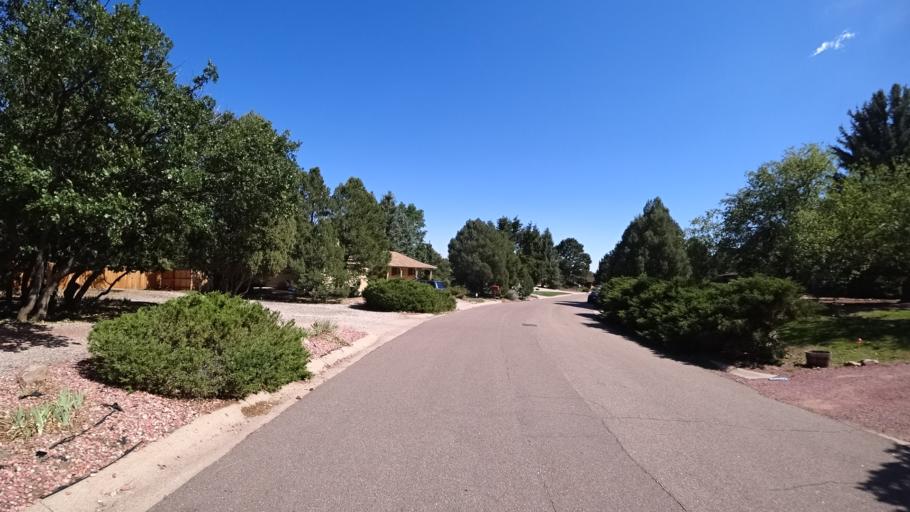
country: US
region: Colorado
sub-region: El Paso County
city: Colorado Springs
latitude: 38.8134
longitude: -104.8629
